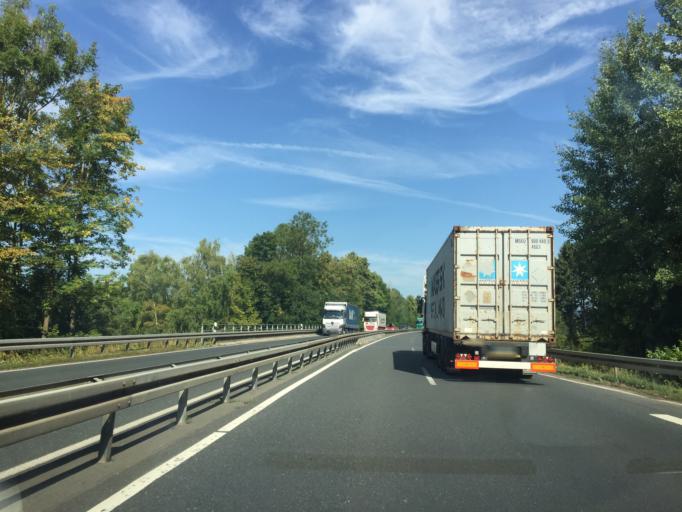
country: DE
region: Lower Saxony
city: Windhausen
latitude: 51.7817
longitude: 10.2020
